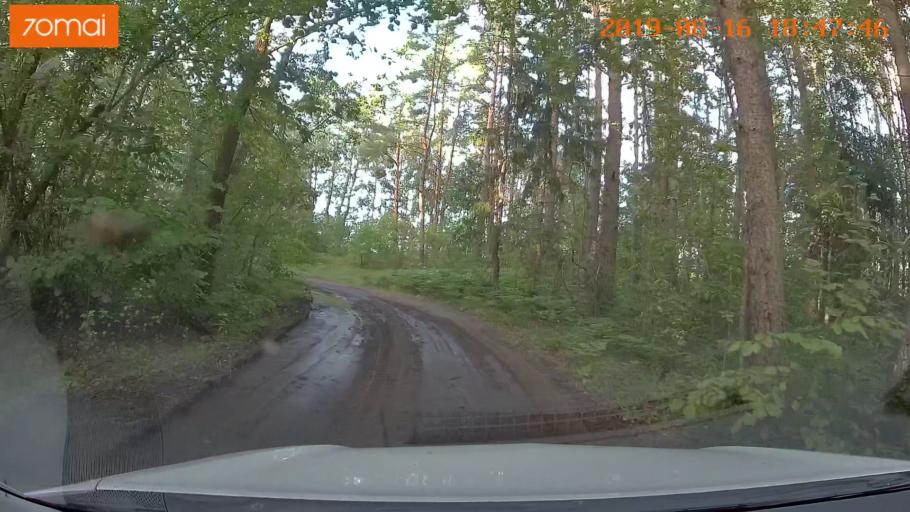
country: BY
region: Mogilev
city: Asipovichy
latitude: 53.2311
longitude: 28.6681
